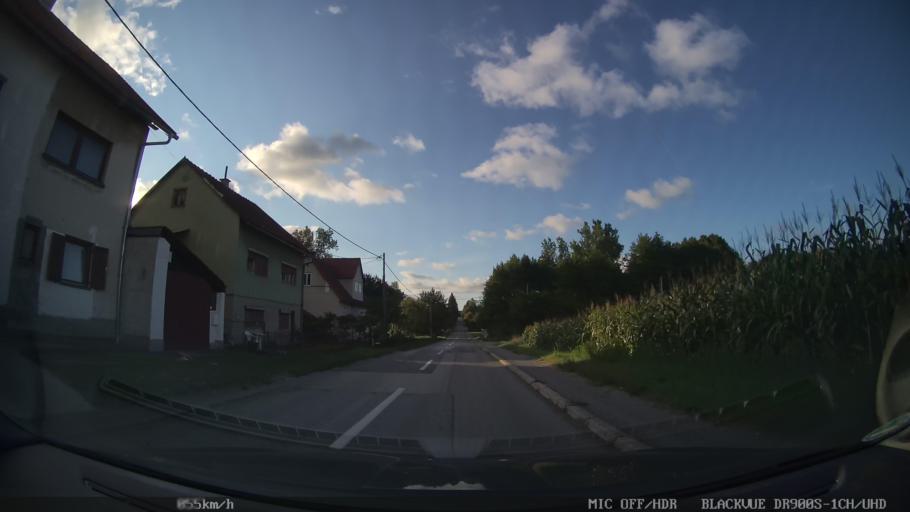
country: HR
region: Karlovacka
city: Plaski
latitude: 45.0783
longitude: 15.3643
